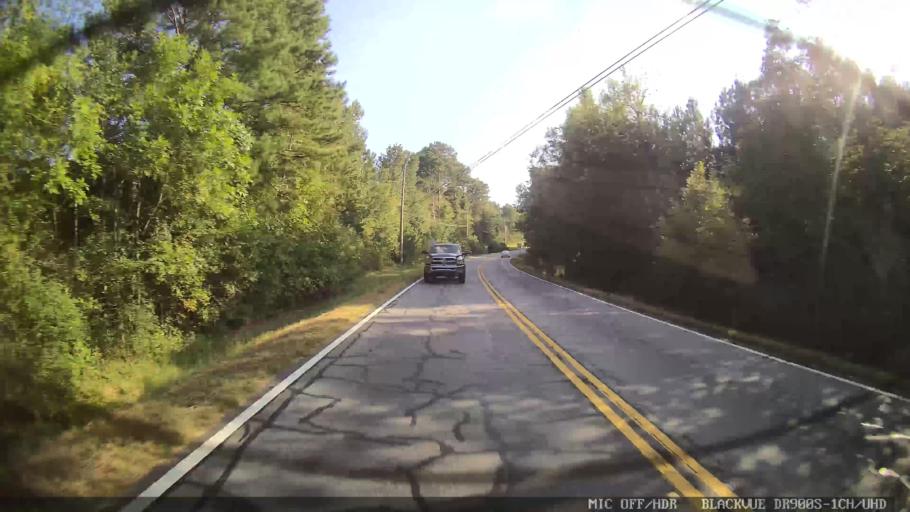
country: US
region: Georgia
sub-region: Murray County
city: Chatsworth
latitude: 34.7013
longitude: -84.8198
